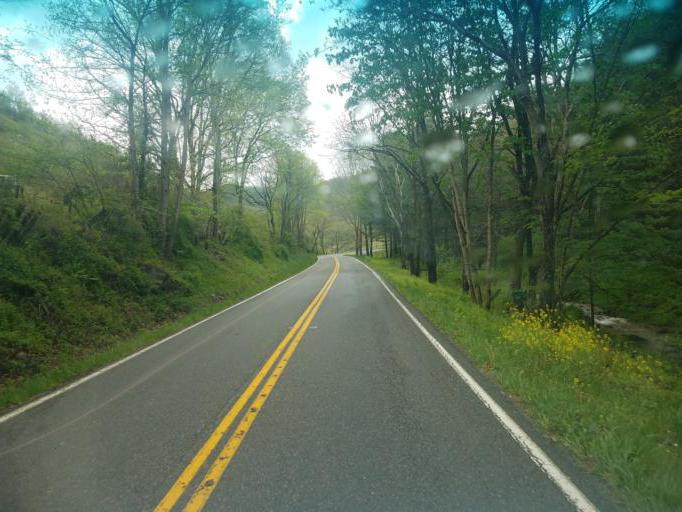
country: US
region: Virginia
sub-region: Smyth County
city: Marion
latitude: 36.9390
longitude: -81.5275
